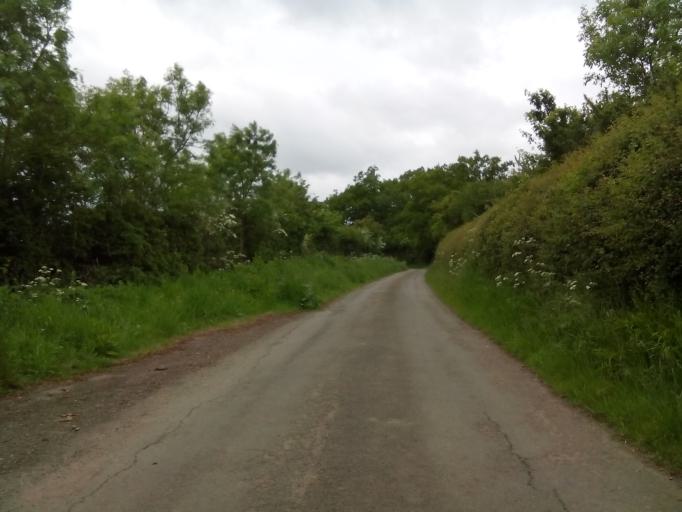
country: GB
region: England
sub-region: District of Rutland
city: Morcott
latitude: 52.5374
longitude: -0.6006
